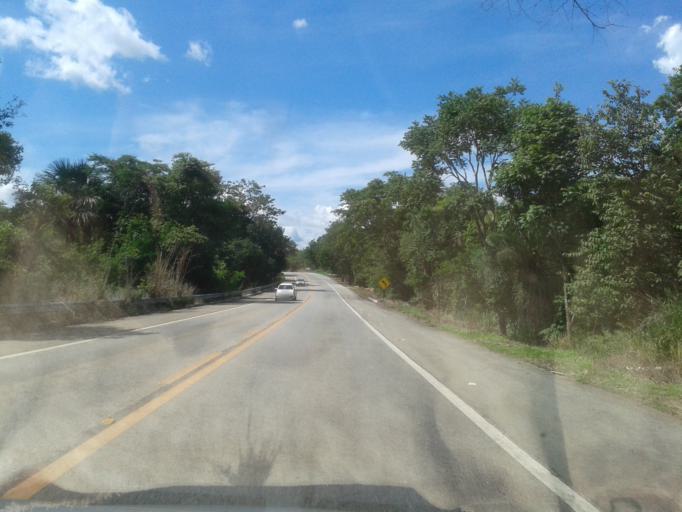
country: BR
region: Goias
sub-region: Goias
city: Goias
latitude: -15.7193
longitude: -50.1882
